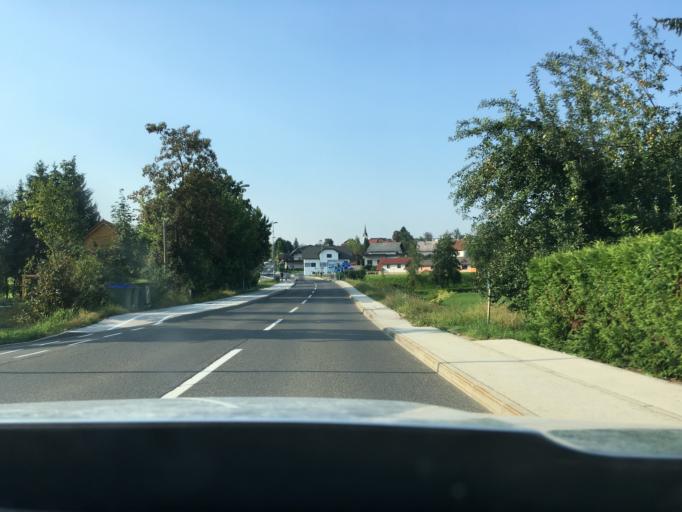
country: SI
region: Novo Mesto
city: Novo Mesto
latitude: 45.7874
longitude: 15.1796
